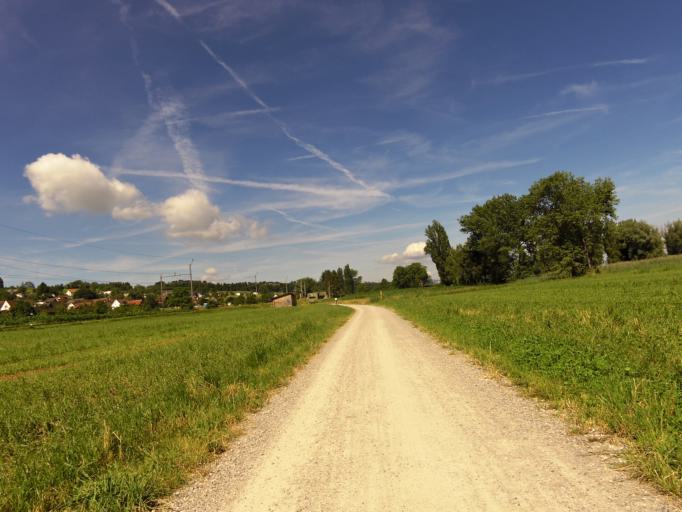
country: CH
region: Thurgau
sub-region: Kreuzlingen District
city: Tagerwilen
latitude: 47.6633
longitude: 9.1151
